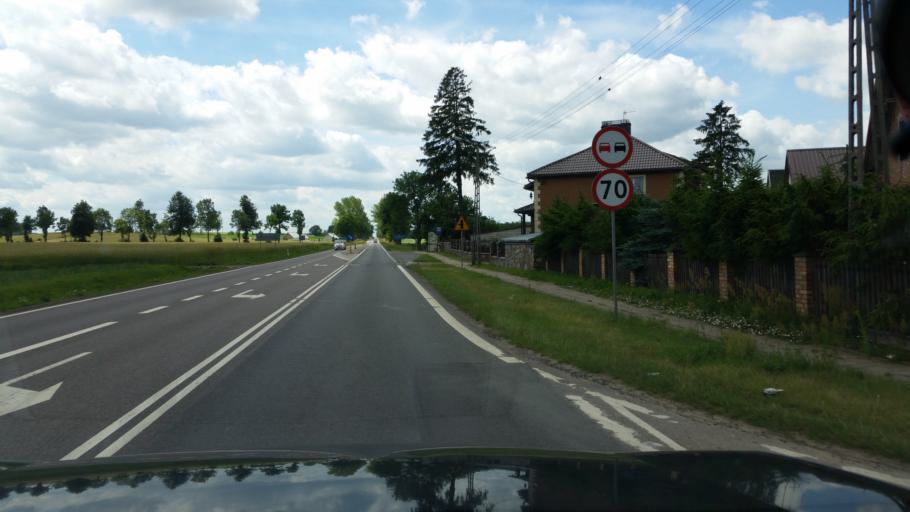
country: PL
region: Podlasie
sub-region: Powiat kolnenski
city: Stawiski
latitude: 53.4619
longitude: 22.1971
